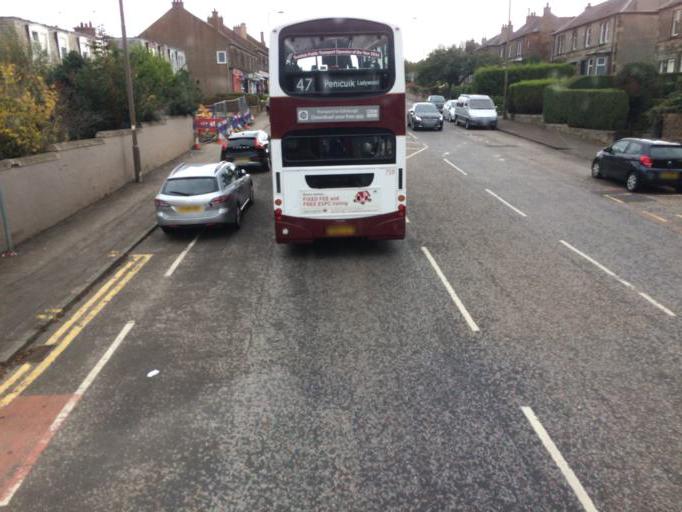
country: GB
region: Scotland
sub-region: Midlothian
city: Loanhead
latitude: 55.9156
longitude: -3.1664
